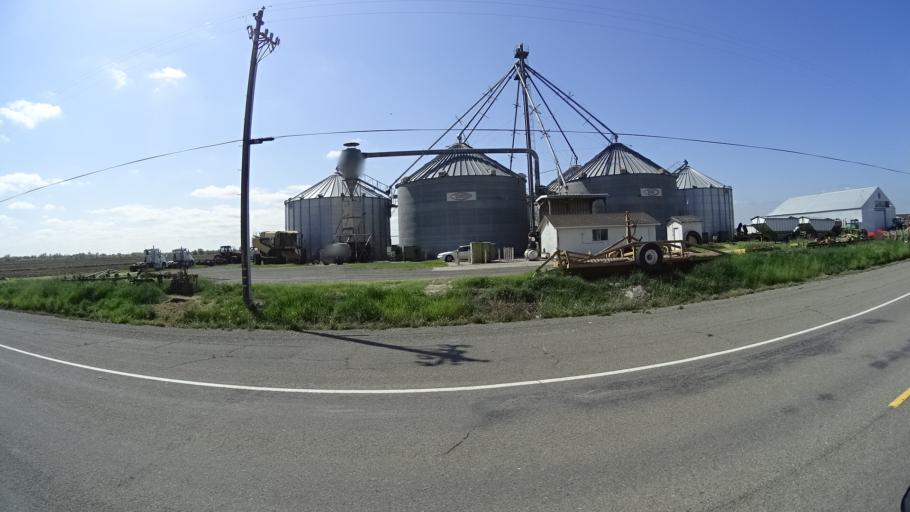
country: US
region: California
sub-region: Butte County
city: Biggs
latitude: 39.4639
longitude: -121.9044
